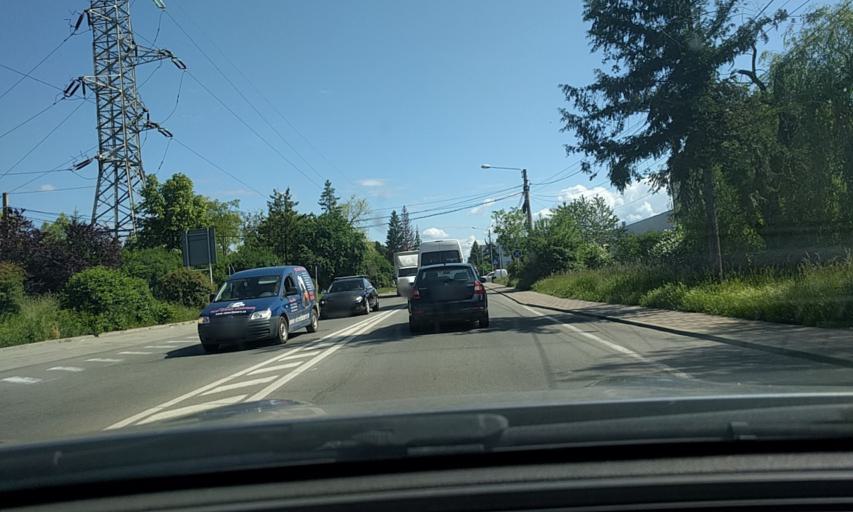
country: RO
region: Bistrita-Nasaud
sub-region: Municipiul Bistrita
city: Viisoara
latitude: 47.1288
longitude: 24.4682
